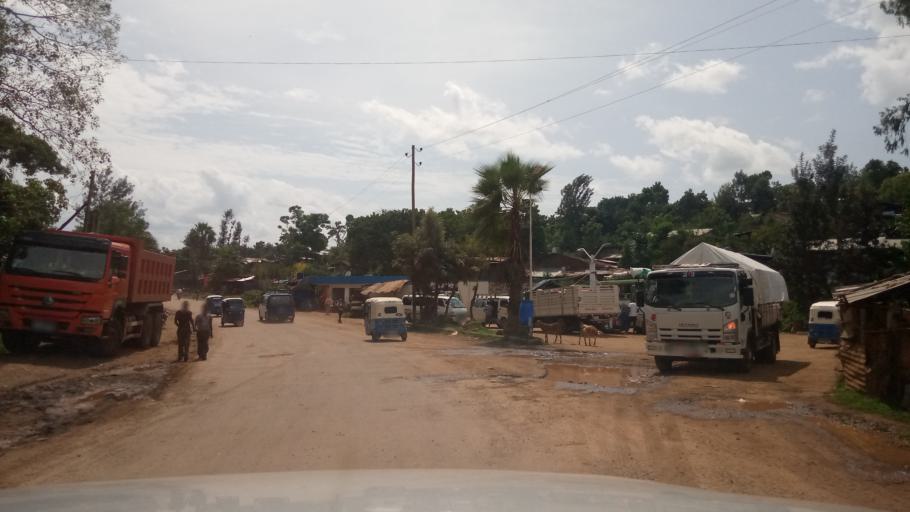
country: ET
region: Oromiya
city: Agaro
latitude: 7.8542
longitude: 36.5924
